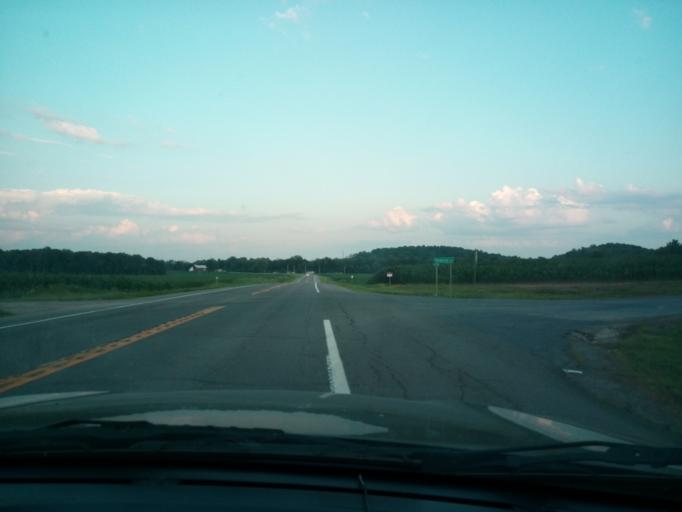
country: US
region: New York
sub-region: Wayne County
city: Clyde
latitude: 43.0710
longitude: -76.7761
